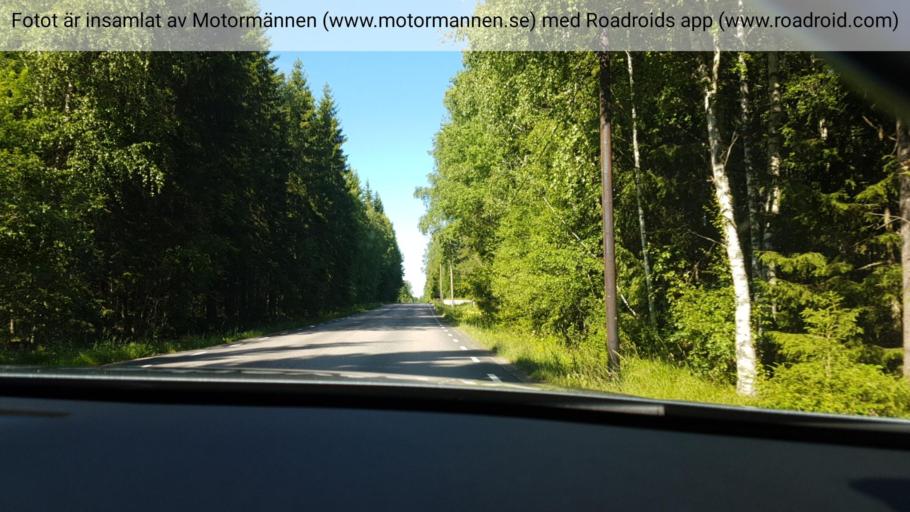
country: SE
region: Vaestra Goetaland
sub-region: Ulricehamns Kommun
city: Ulricehamn
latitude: 57.8586
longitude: 13.4116
